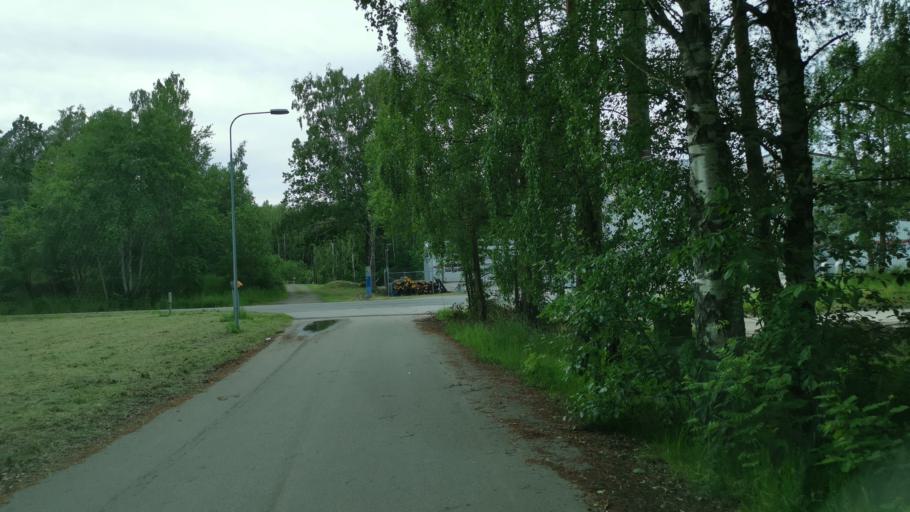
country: SE
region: Vaestra Goetaland
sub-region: Vanersborgs Kommun
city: Vargon
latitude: 58.3579
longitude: 12.3719
